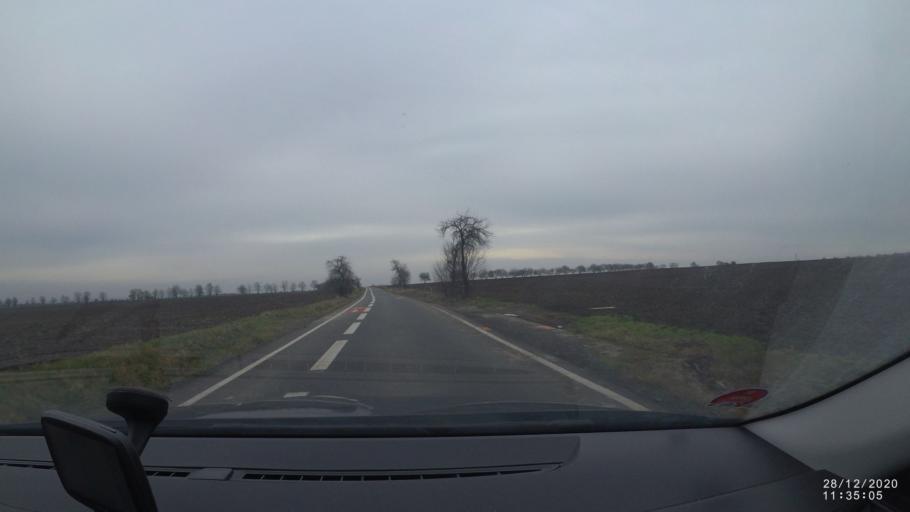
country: CZ
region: Praha
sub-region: Praha 19
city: Satalice
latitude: 50.1310
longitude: 14.5924
